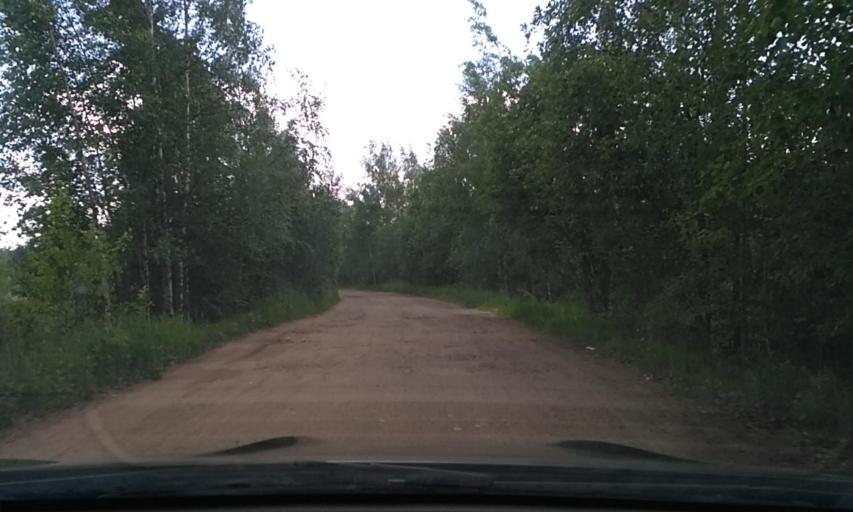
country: RU
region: Leningrad
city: Otradnoye
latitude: 59.8178
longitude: 30.8255
